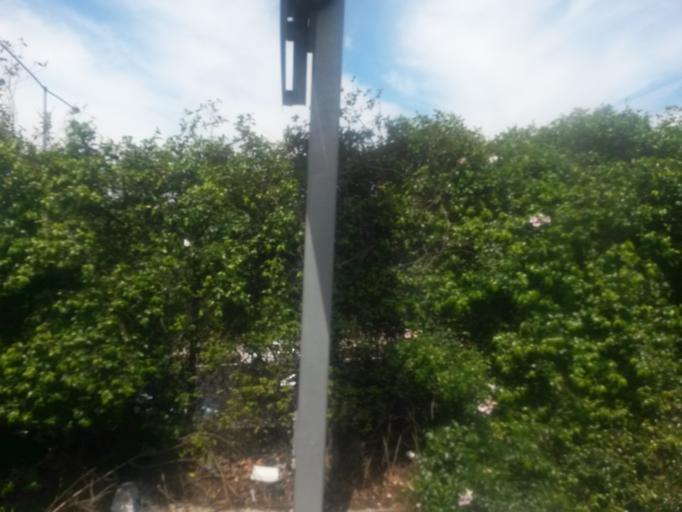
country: AU
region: Victoria
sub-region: Stonnington
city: Toorak
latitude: -37.8304
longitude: 145.0108
